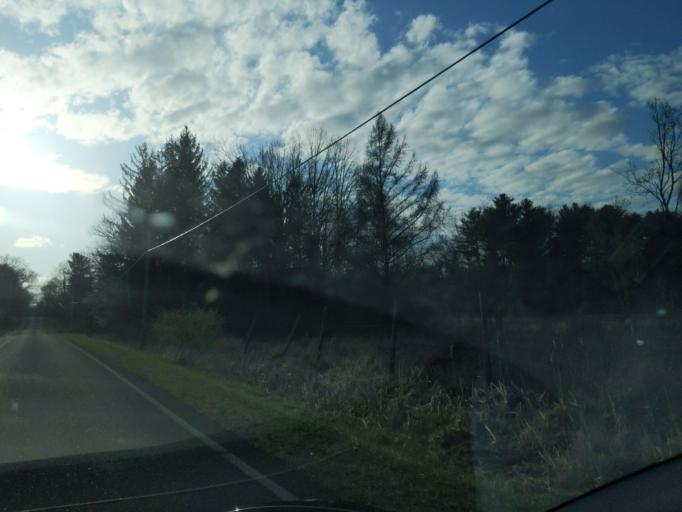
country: US
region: Michigan
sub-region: Ingham County
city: Leslie
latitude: 42.3933
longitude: -84.4367
